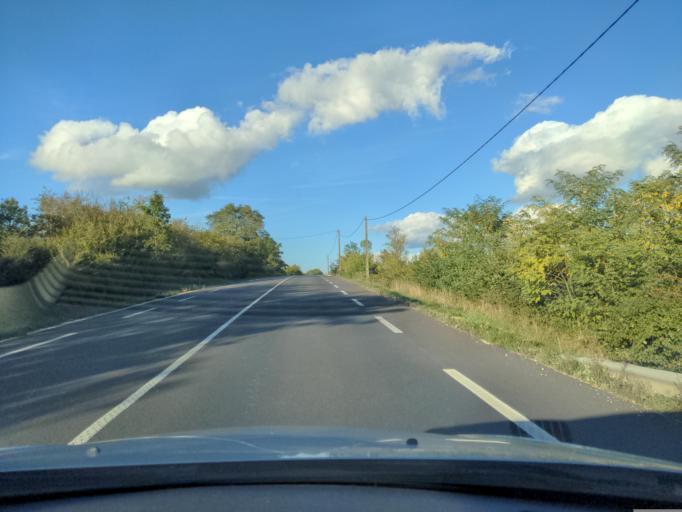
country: FR
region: Bourgogne
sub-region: Departement de la Cote-d'Or
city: Saint-Julien
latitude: 47.4400
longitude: 5.1137
